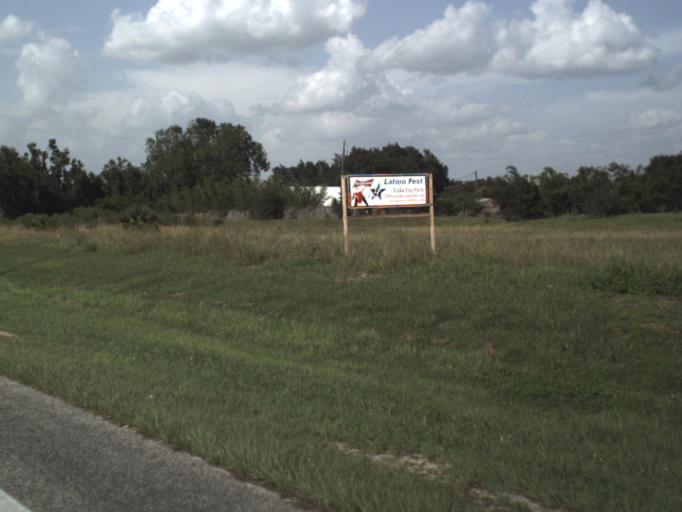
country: US
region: Florida
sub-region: Polk County
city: Lake Hamilton
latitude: 28.0828
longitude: -81.6496
